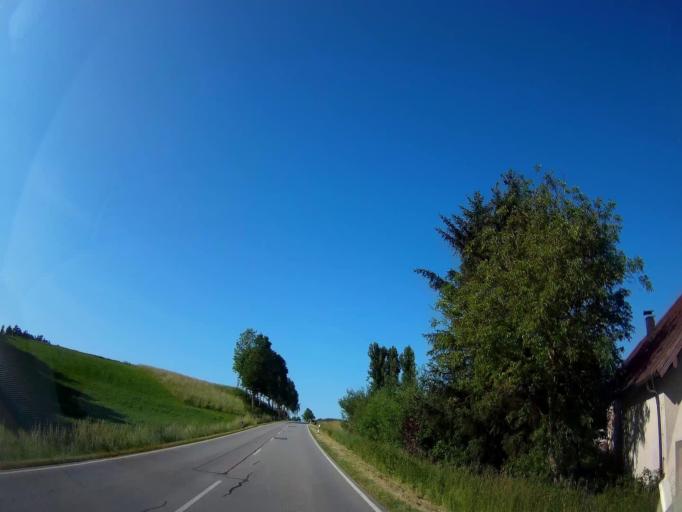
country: DE
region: Bavaria
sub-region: Lower Bavaria
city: Zeilarn
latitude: 48.3102
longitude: 12.8286
